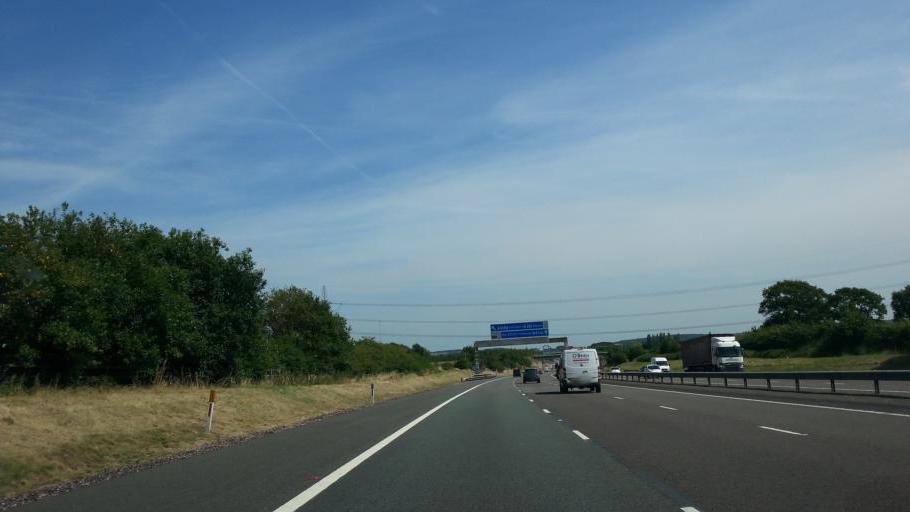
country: GB
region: England
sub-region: Staffordshire
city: Shenstone
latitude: 52.6524
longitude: -1.8478
